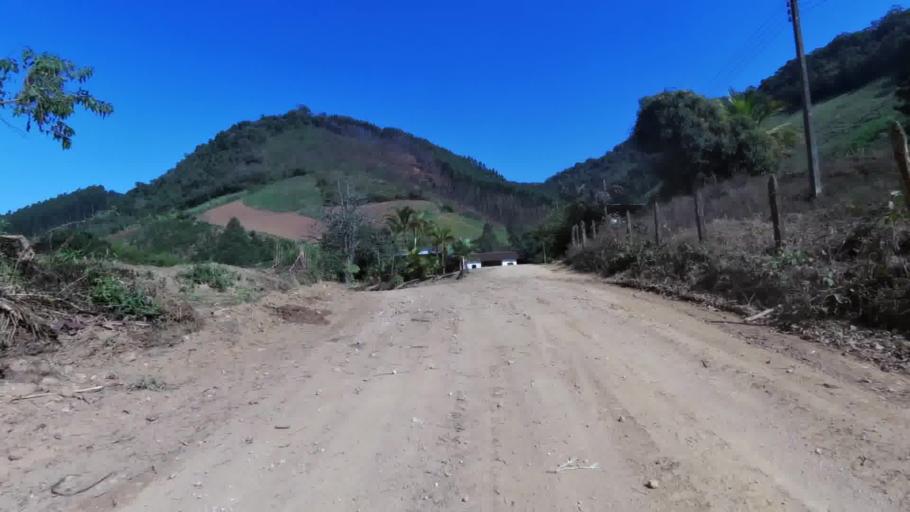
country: BR
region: Espirito Santo
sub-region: Alfredo Chaves
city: Alfredo Chaves
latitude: -20.5323
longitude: -40.8458
